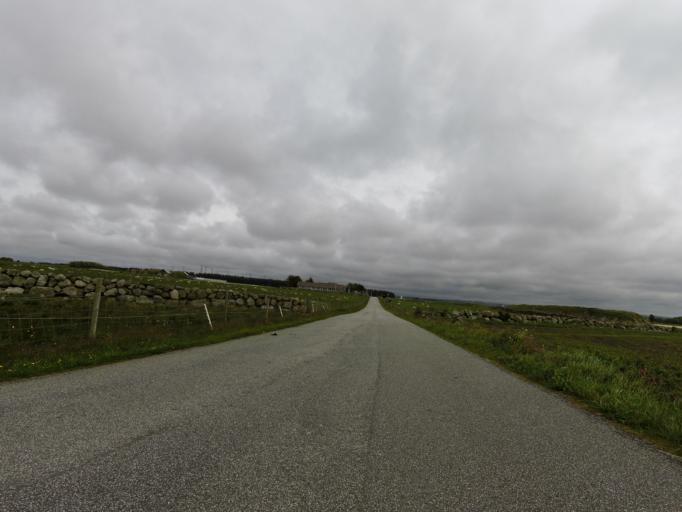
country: NO
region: Rogaland
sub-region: Ha
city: Naerbo
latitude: 58.6528
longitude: 5.5850
